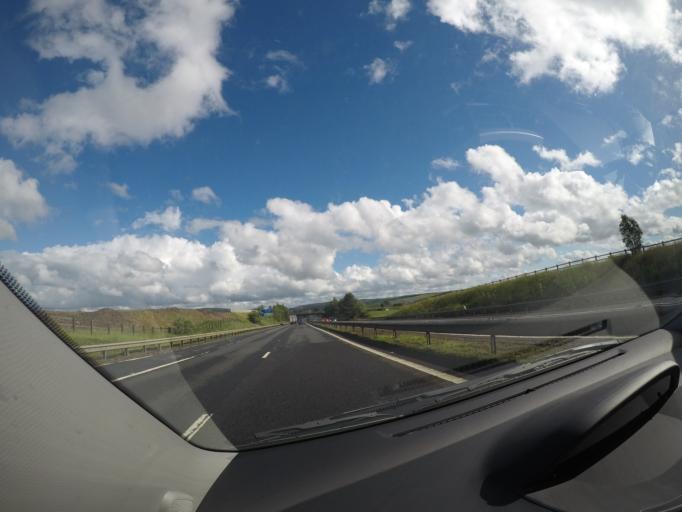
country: GB
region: Scotland
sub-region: South Lanarkshire
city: Douglas
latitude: 55.6008
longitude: -3.8368
